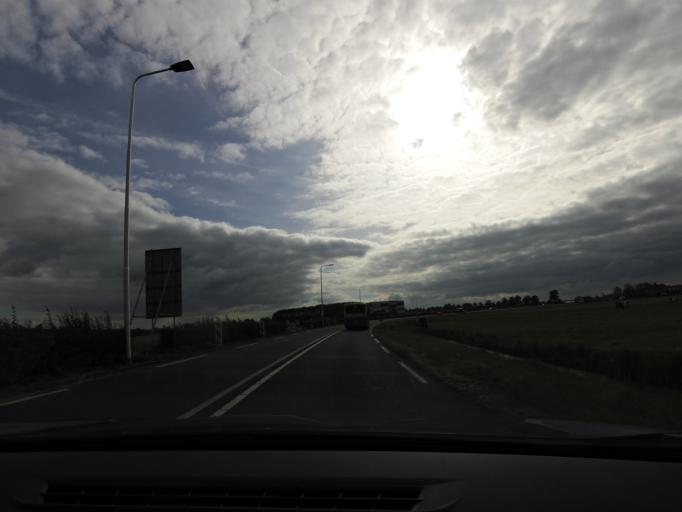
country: NL
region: Utrecht
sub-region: Gemeente Lopik
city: Lopik
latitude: 51.9779
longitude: 4.9784
